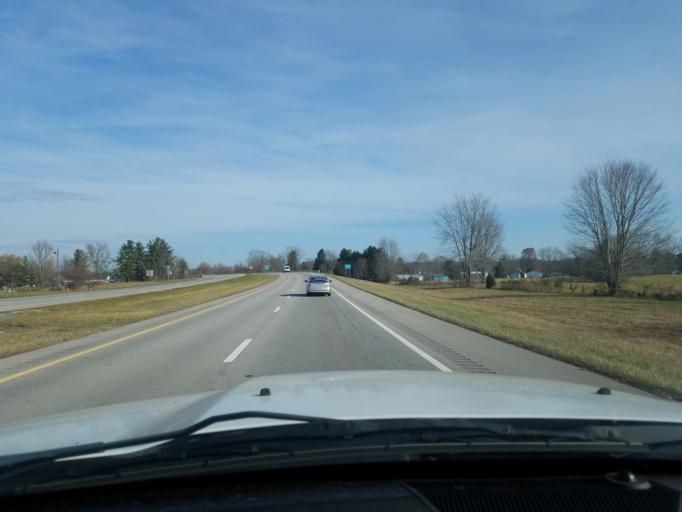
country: US
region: Ohio
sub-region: Athens County
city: Athens
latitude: 39.2230
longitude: -82.2039
